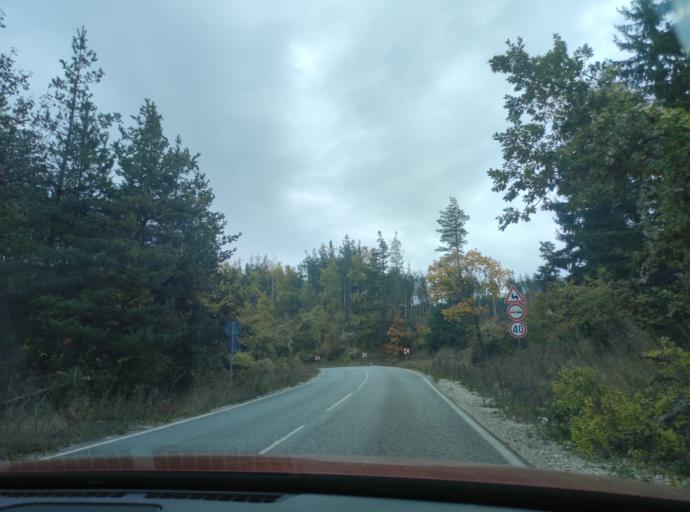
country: BG
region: Sofiya
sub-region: Obshtina Godech
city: Godech
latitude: 43.0184
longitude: 23.1298
